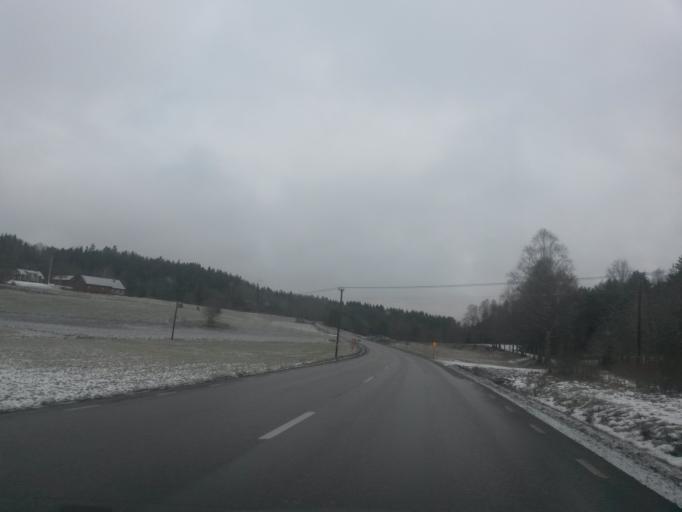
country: SE
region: Vaestra Goetaland
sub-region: Vargarda Kommun
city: Jonstorp
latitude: 58.0646
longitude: 12.6817
